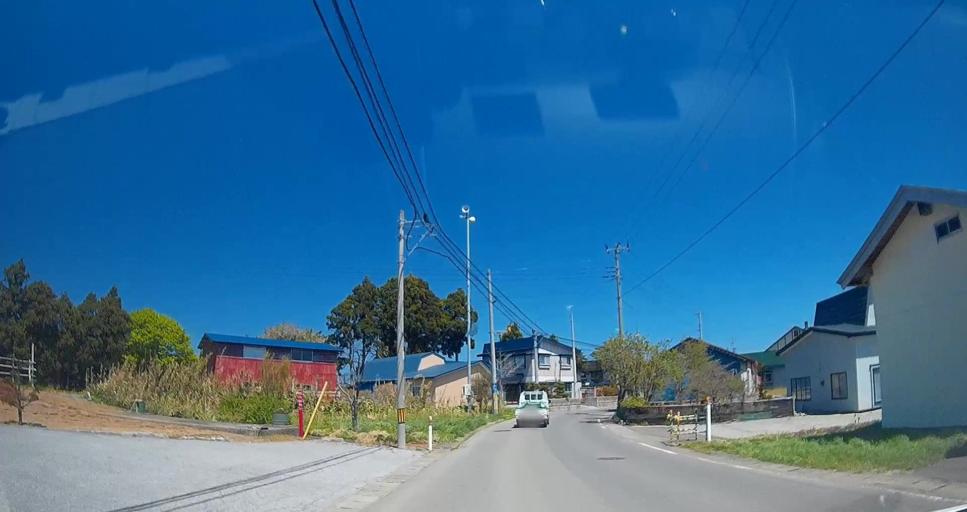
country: JP
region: Aomori
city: Mutsu
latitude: 41.2275
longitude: 141.3941
